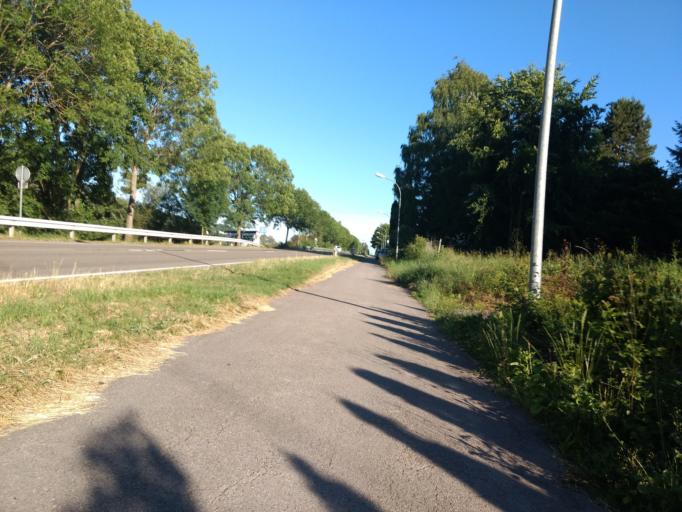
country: DE
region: Saarland
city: Merzig
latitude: 49.4024
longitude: 6.6531
